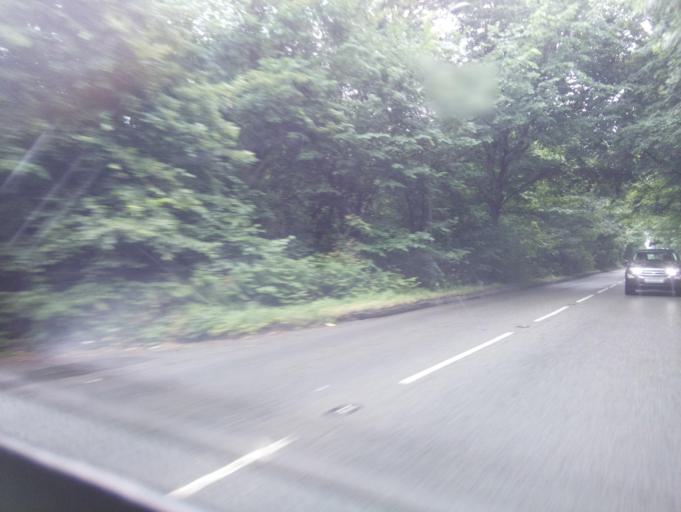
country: GB
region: England
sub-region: Surrey
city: Redhill
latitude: 51.2231
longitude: -0.1727
